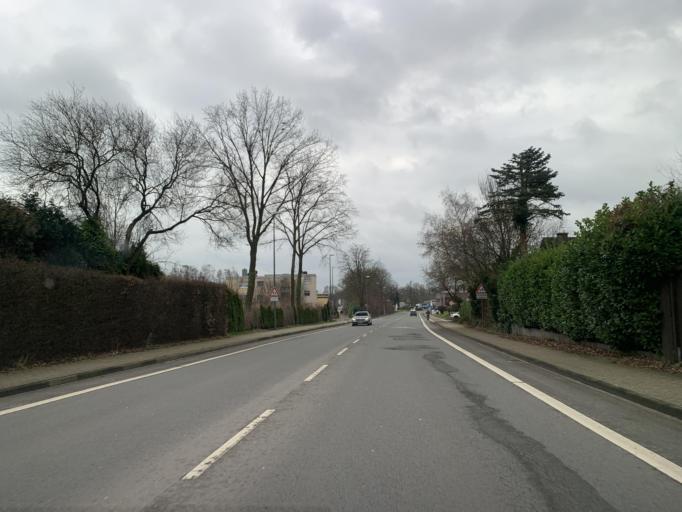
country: DE
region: North Rhine-Westphalia
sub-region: Regierungsbezirk Munster
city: Dulmen
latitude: 51.8334
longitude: 7.2961
